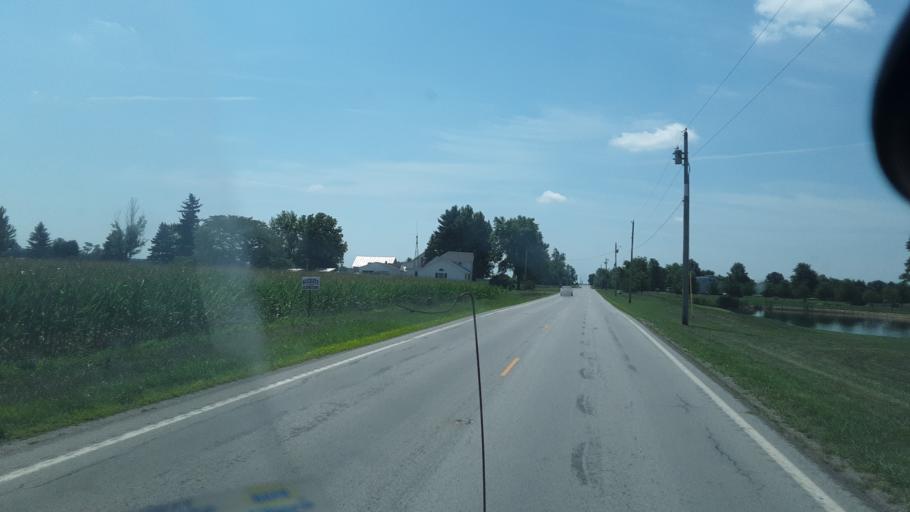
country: US
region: Ohio
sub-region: Hancock County
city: Arlington
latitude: 40.9639
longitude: -83.5746
